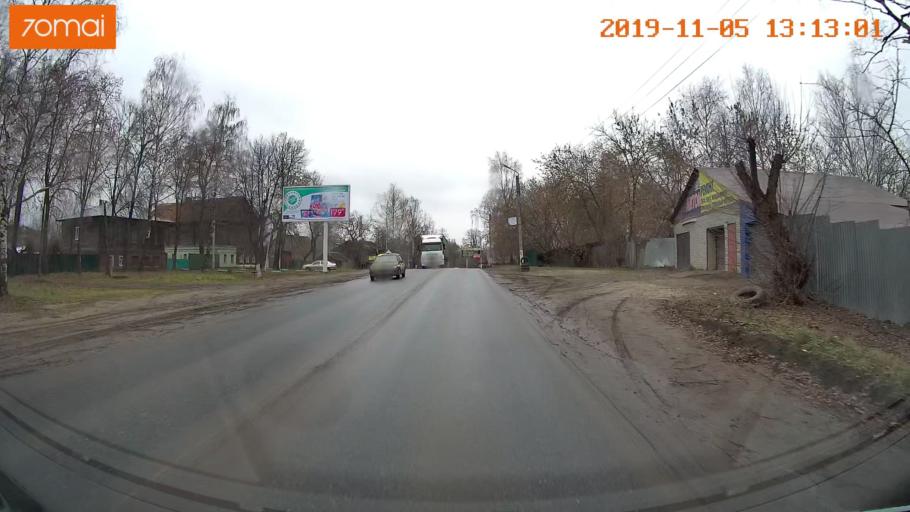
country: RU
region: Ivanovo
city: Shuya
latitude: 56.8538
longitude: 41.3532
